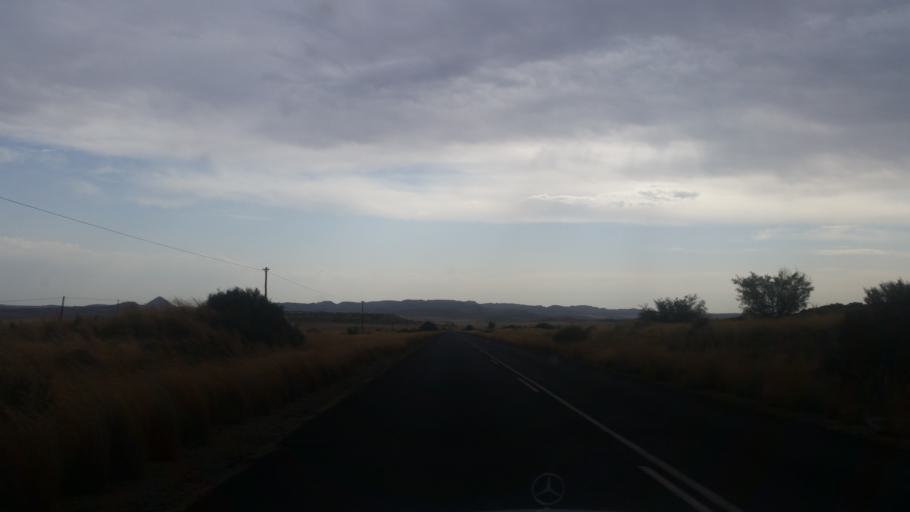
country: ZA
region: Orange Free State
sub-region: Xhariep District Municipality
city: Trompsburg
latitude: -30.4214
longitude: 26.1767
